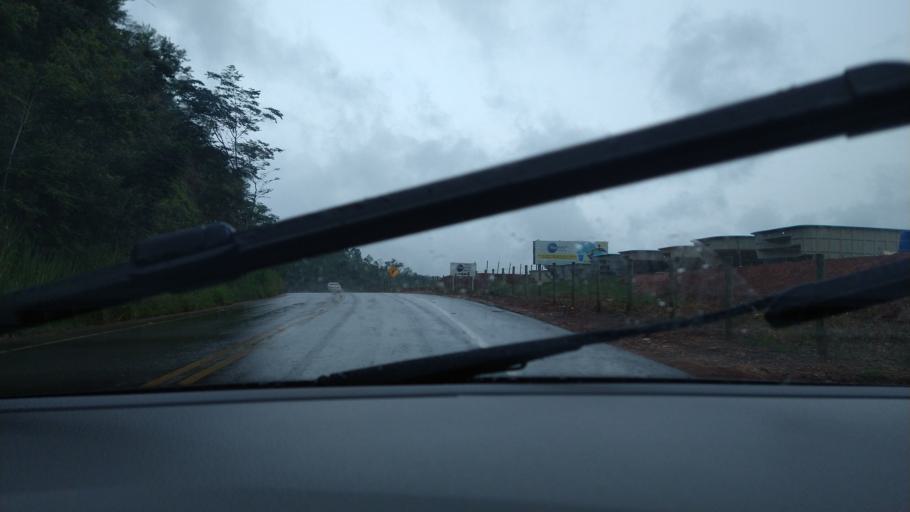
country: BR
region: Minas Gerais
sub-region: Vicosa
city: Vicosa
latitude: -20.6111
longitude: -42.8682
